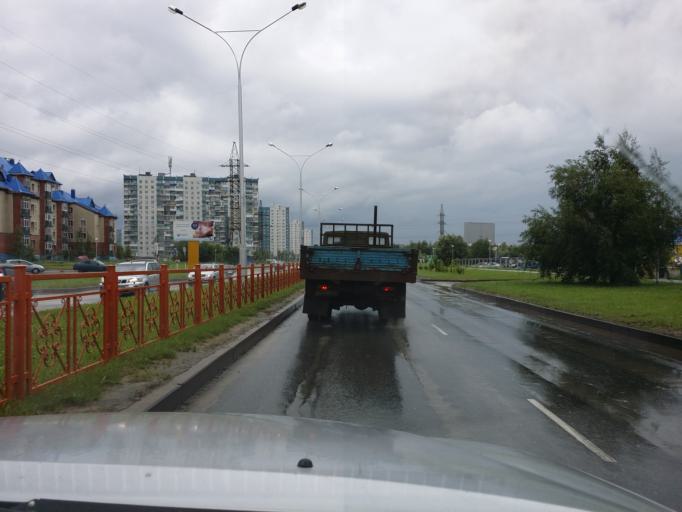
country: RU
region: Khanty-Mansiyskiy Avtonomnyy Okrug
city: Nizhnevartovsk
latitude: 60.9560
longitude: 76.5723
